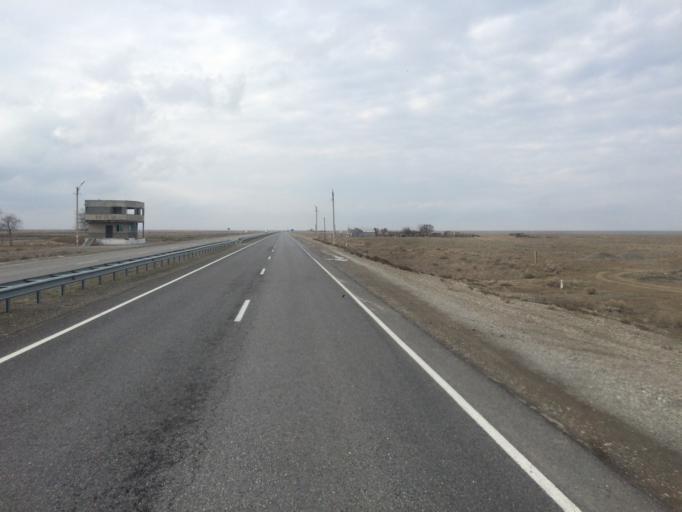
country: KZ
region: Ongtustik Qazaqstan
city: Turkestan
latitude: 43.5260
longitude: 67.7932
